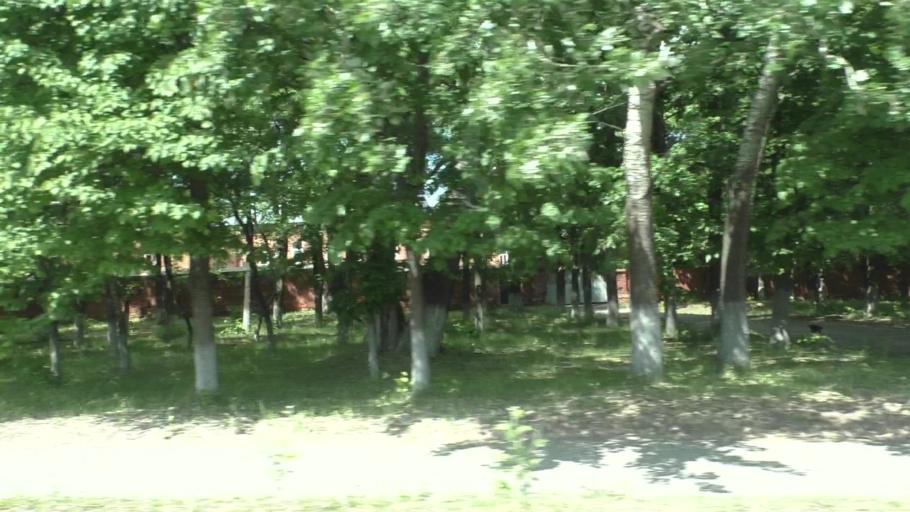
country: RU
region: Moskovskaya
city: Yegor'yevsk
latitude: 55.3873
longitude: 39.0328
